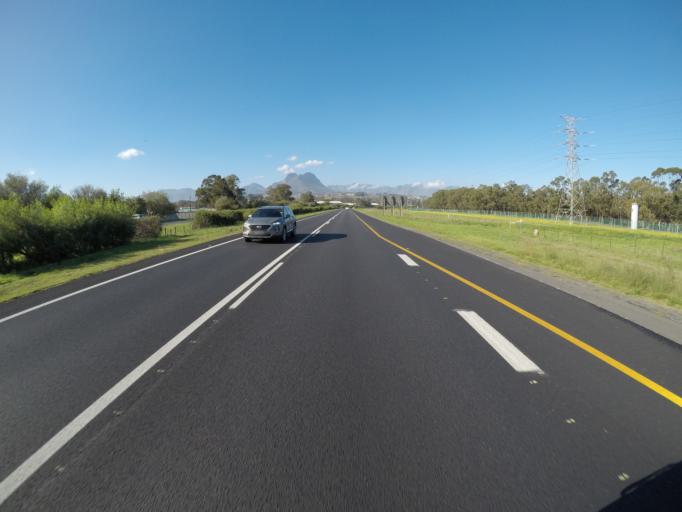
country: ZA
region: Western Cape
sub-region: Cape Winelands District Municipality
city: Stellenbosch
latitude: -34.0589
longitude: 18.7862
